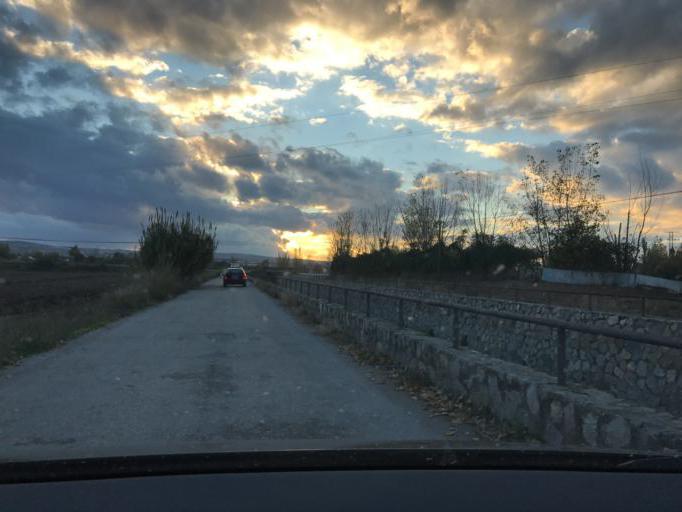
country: ES
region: Andalusia
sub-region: Provincia de Granada
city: Churriana de la Vega
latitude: 37.1723
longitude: -3.6468
